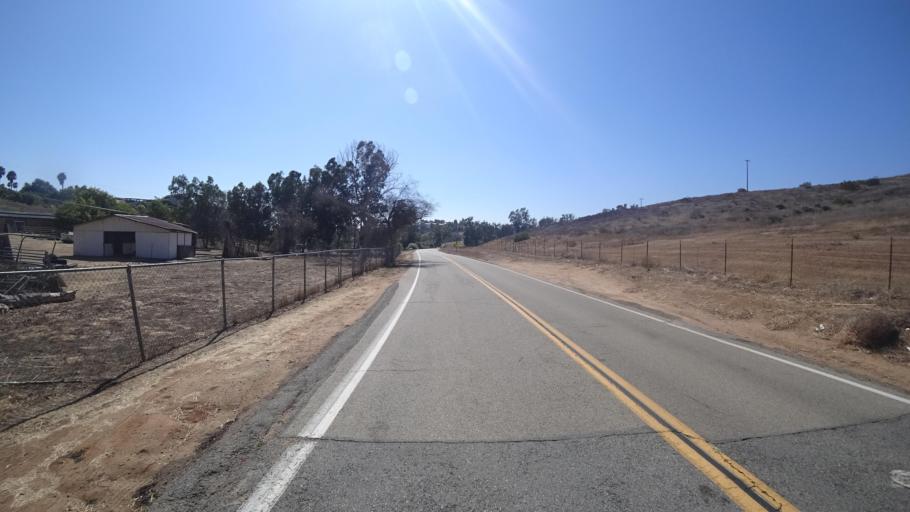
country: US
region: California
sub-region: San Diego County
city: Bonsall
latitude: 33.2972
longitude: -117.2033
